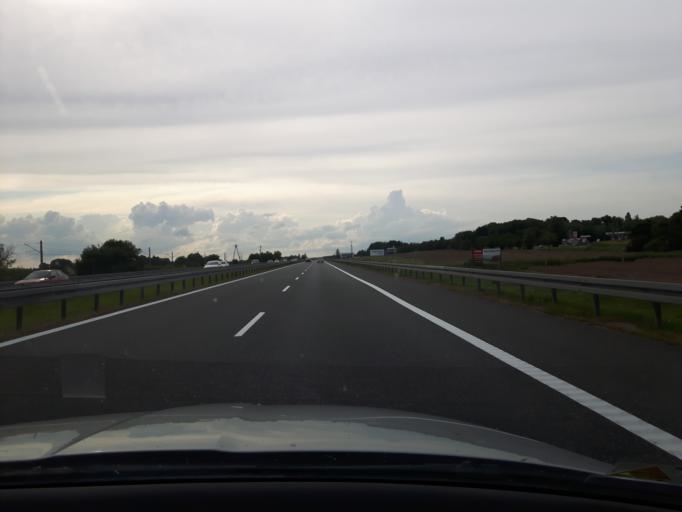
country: PL
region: Warmian-Masurian Voivodeship
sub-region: Powiat elblaski
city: Gronowo Gorne
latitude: 54.1066
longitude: 19.5035
